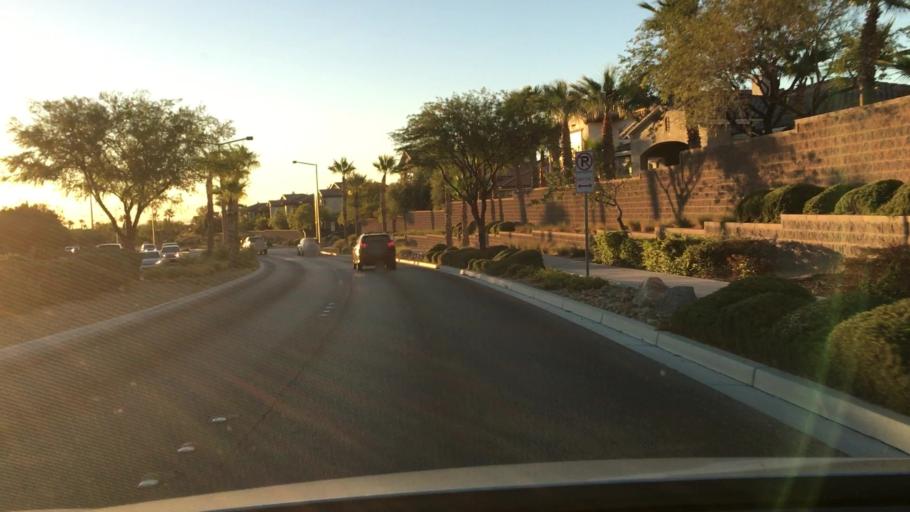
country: US
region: Nevada
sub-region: Clark County
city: Summerlin South
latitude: 36.1560
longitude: -115.3505
